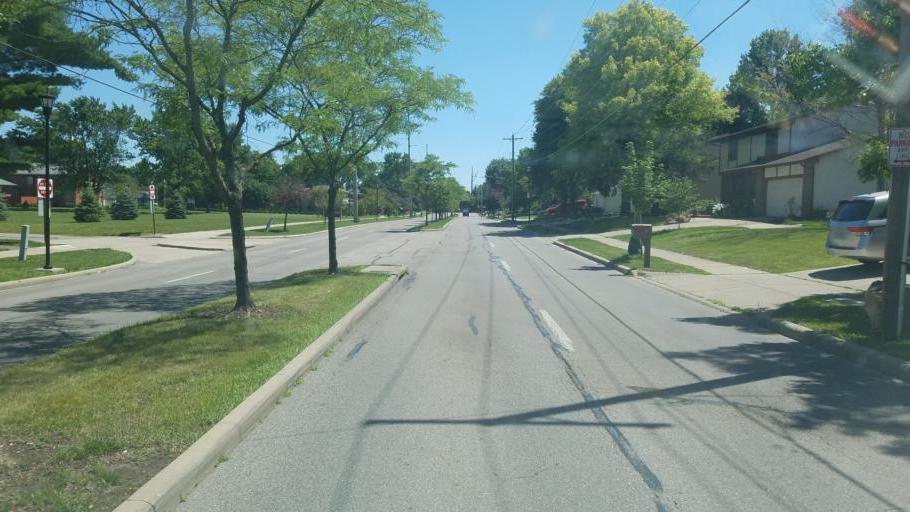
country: US
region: Ohio
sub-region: Franklin County
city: Westerville
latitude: 40.1228
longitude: -82.9036
